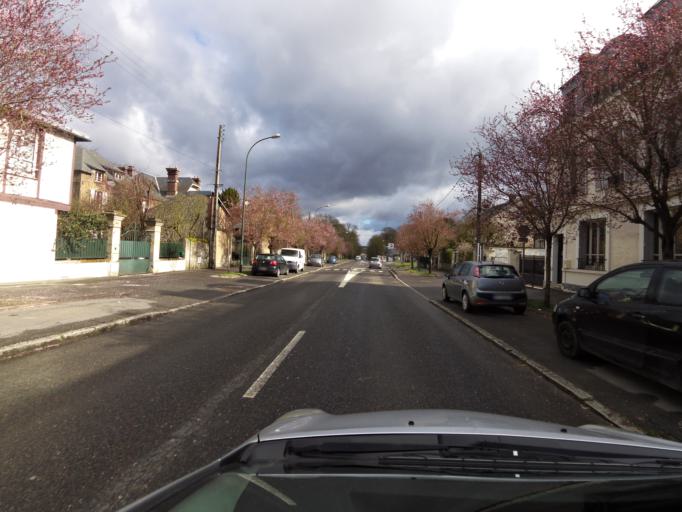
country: FR
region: Picardie
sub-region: Departement de l'Oise
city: Senlis
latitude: 49.2099
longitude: 2.5921
